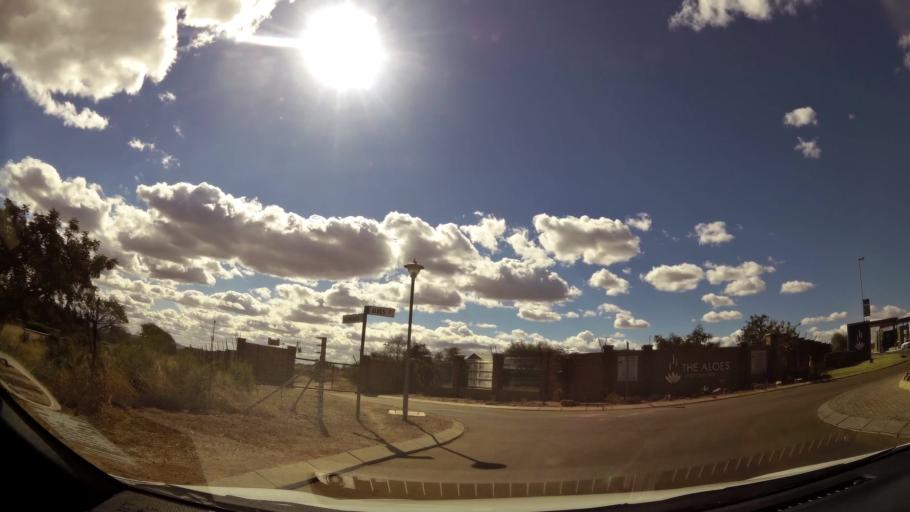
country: ZA
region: Limpopo
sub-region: Capricorn District Municipality
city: Polokwane
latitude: -23.8695
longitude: 29.4963
